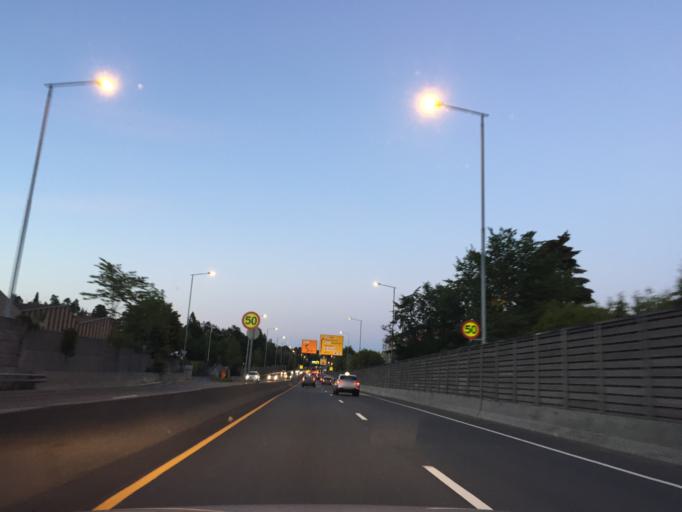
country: NO
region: Oslo
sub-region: Oslo
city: Sjolyststranda
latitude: 59.9329
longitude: 10.6713
